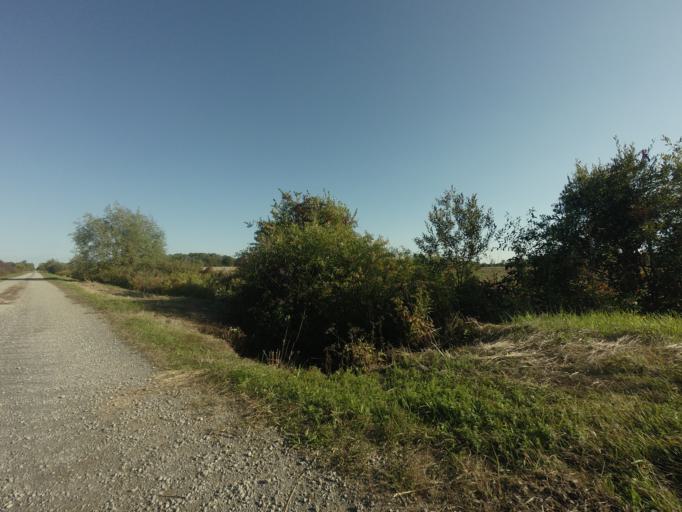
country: CA
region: Ontario
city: Hawkesbury
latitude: 45.5324
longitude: -74.5804
